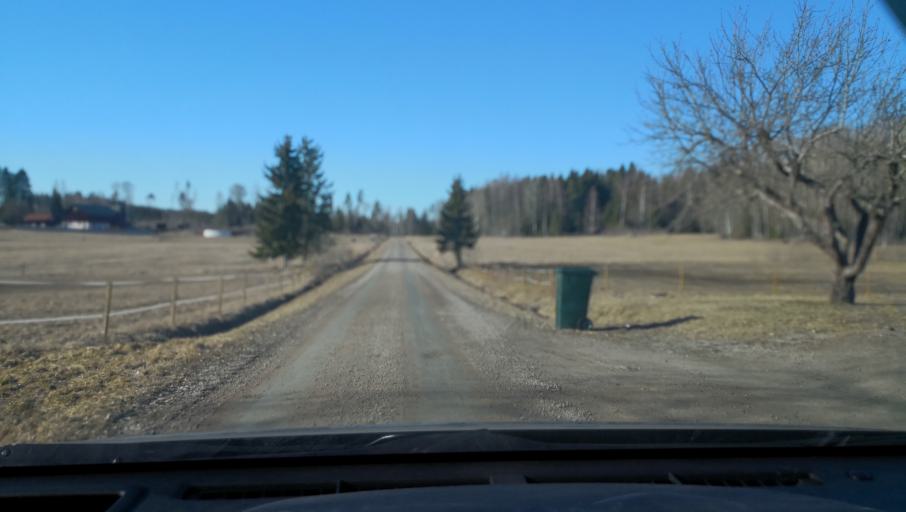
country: SE
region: Dalarna
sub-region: Avesta Kommun
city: Horndal
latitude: 60.1723
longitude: 16.6330
